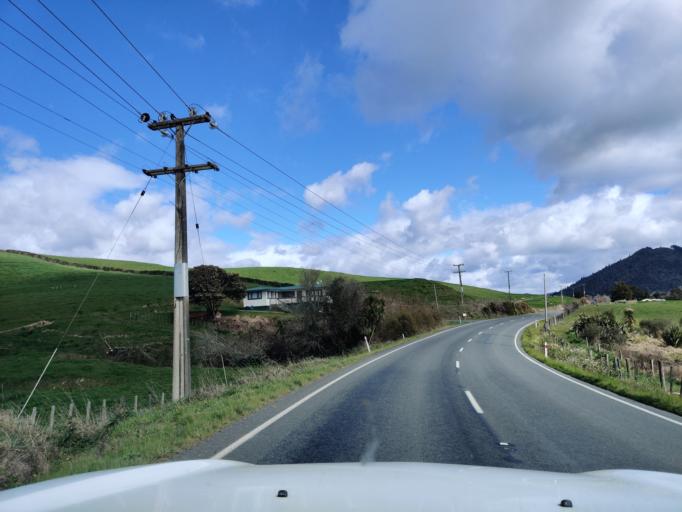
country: NZ
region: Waikato
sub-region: Waikato District
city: Ngaruawahia
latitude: -37.5884
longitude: 175.2142
